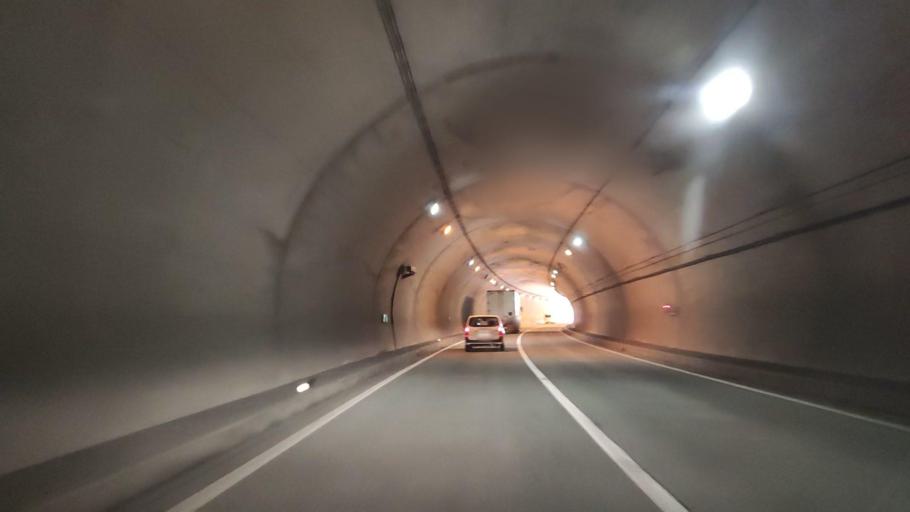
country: JP
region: Toyama
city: Yatsuomachi-higashikumisaka
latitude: 36.5296
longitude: 137.2265
